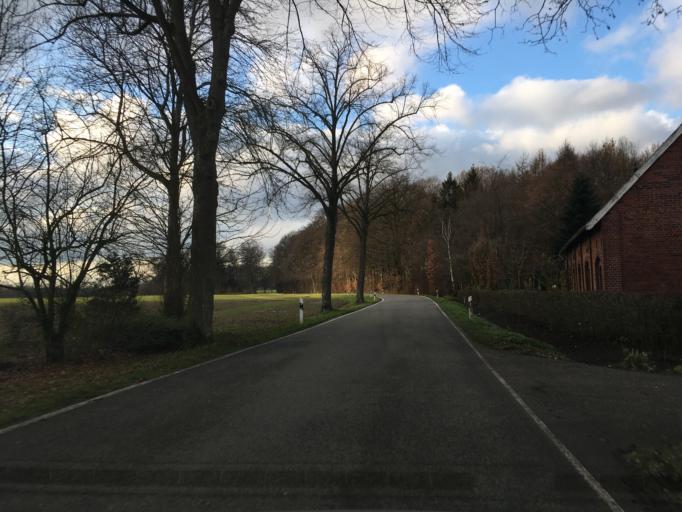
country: DE
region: North Rhine-Westphalia
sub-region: Regierungsbezirk Munster
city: Gescher
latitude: 51.9527
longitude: 7.0712
